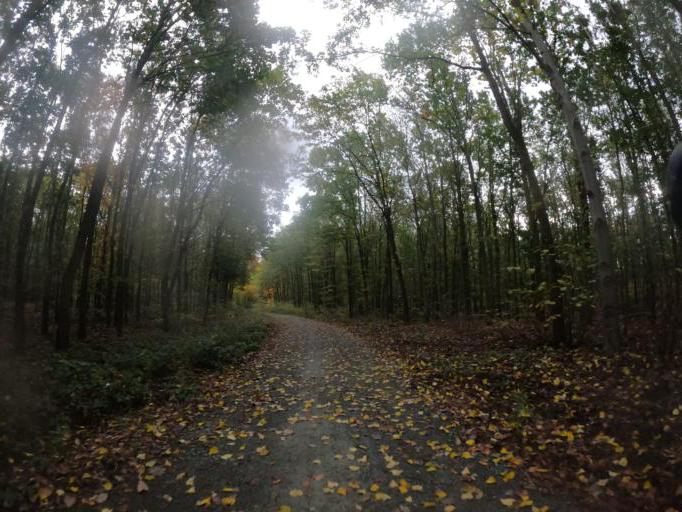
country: DE
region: Hesse
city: Kelsterbach
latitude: 50.0560
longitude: 8.5795
